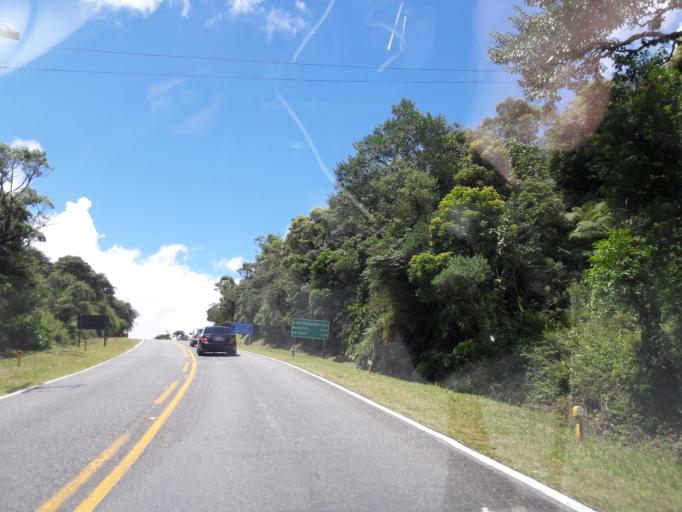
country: BR
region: Parana
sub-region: Campina Grande Do Sul
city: Campina Grande do Sul
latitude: -25.3331
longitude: -48.9072
